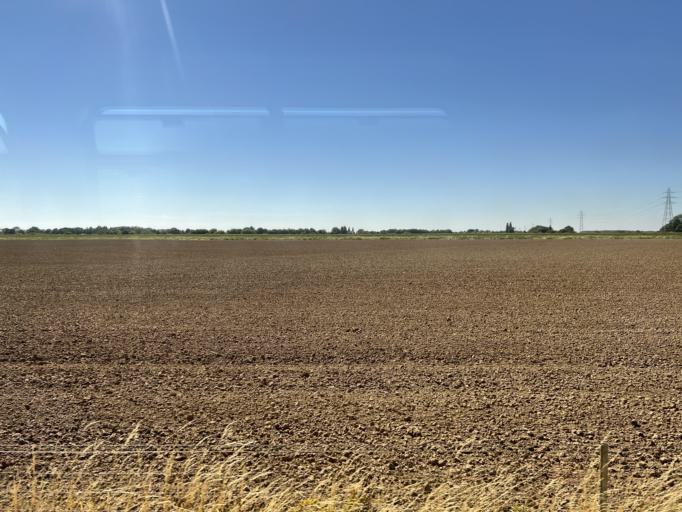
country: GB
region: England
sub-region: Lincolnshire
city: Wainfleet All Saints
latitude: 53.1186
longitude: 0.2060
